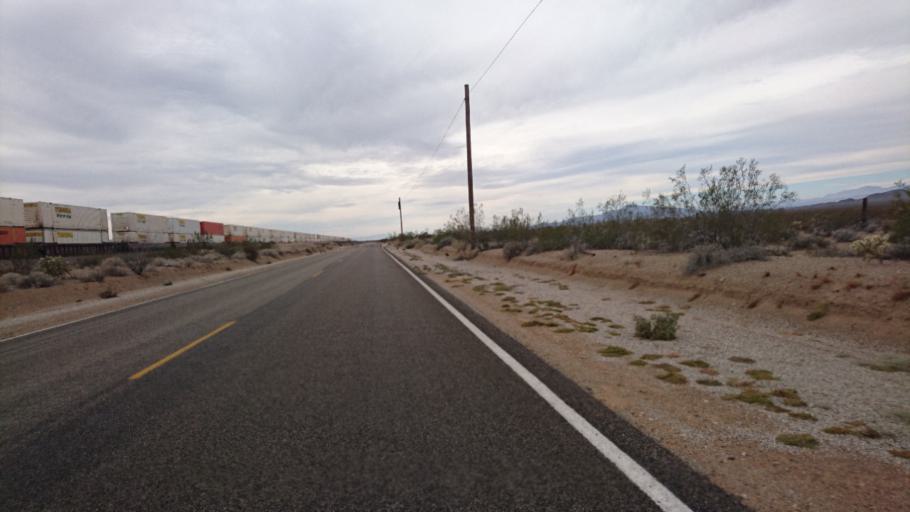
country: US
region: California
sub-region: San Bernardino County
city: Needles
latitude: 34.8799
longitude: -115.1052
